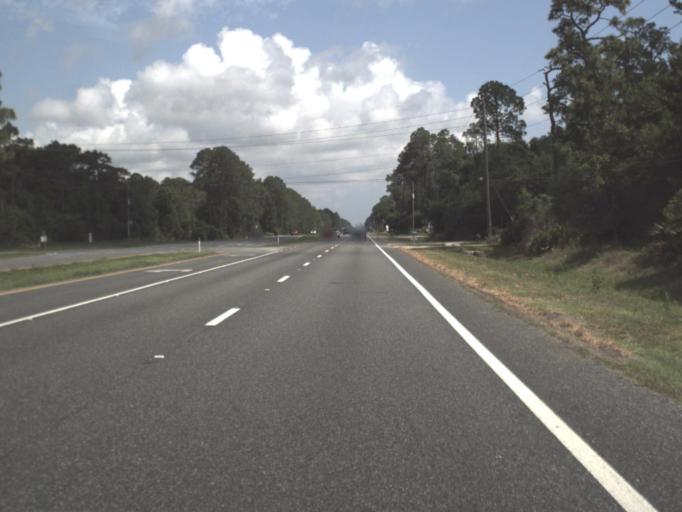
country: US
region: Florida
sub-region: Saint Johns County
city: Saint Augustine Shores
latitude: 29.7776
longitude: -81.3164
